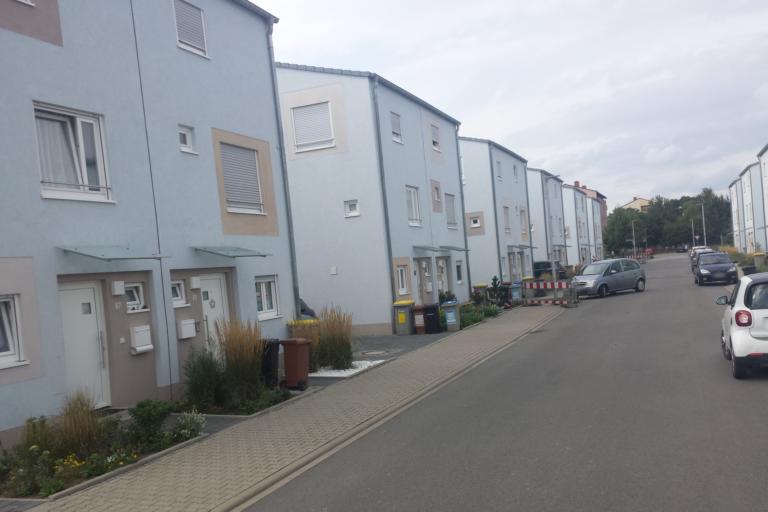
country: DE
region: Baden-Wuerttemberg
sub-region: Karlsruhe Region
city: Mannheim
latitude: 49.5453
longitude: 8.4716
